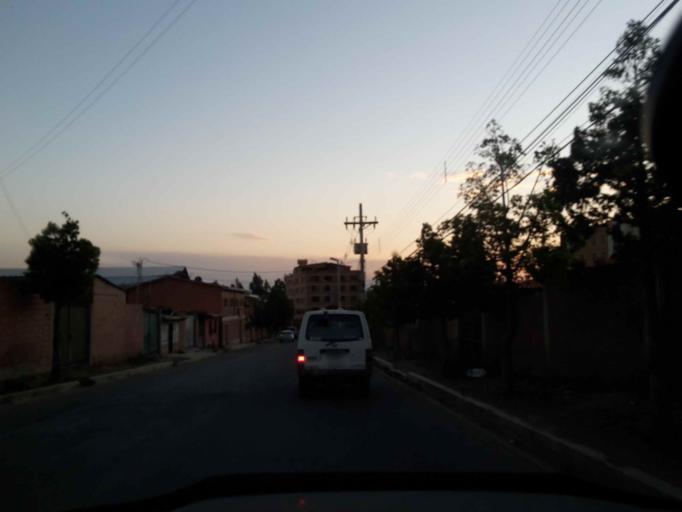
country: BO
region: Cochabamba
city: Cochabamba
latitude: -17.3438
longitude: -66.2041
